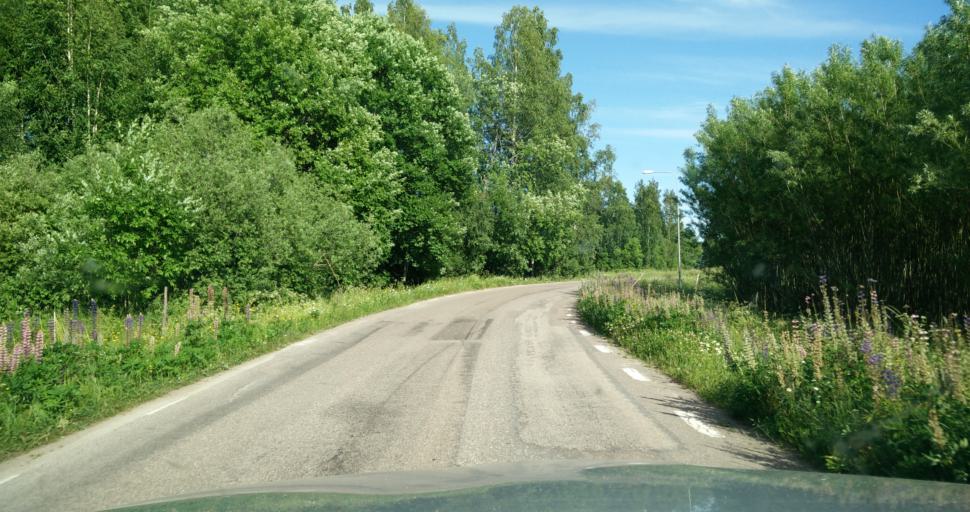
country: SE
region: Dalarna
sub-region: Hedemora Kommun
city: Langshyttan
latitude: 60.3920
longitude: 15.9635
